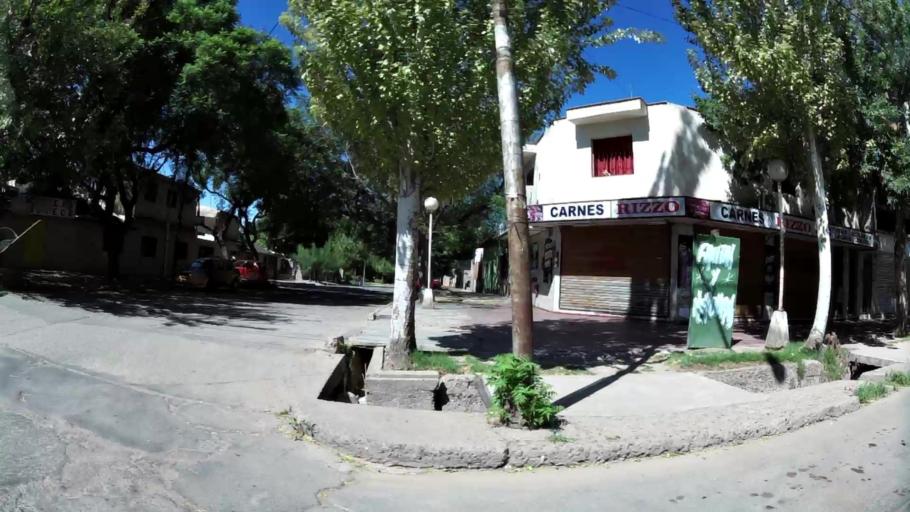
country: AR
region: Mendoza
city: Las Heras
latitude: -32.8483
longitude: -68.8341
